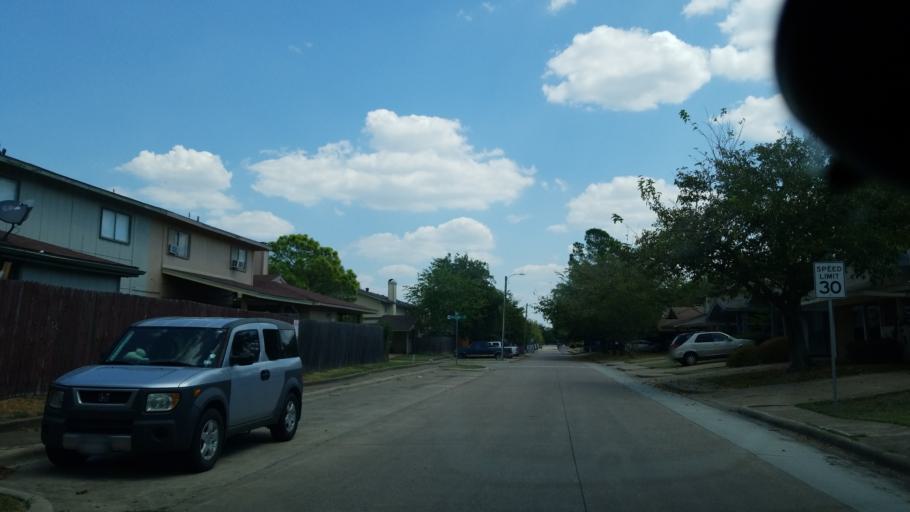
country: US
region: Texas
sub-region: Dallas County
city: Grand Prairie
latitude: 32.7048
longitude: -96.9979
